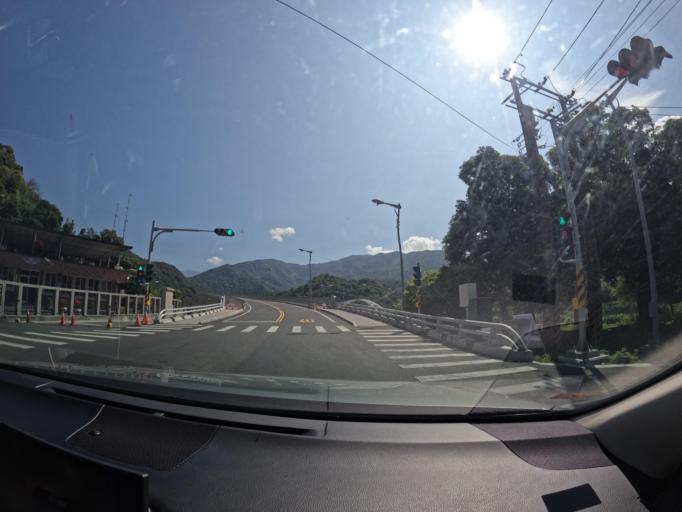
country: TW
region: Taiwan
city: Yujing
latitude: 23.1054
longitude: 120.6940
